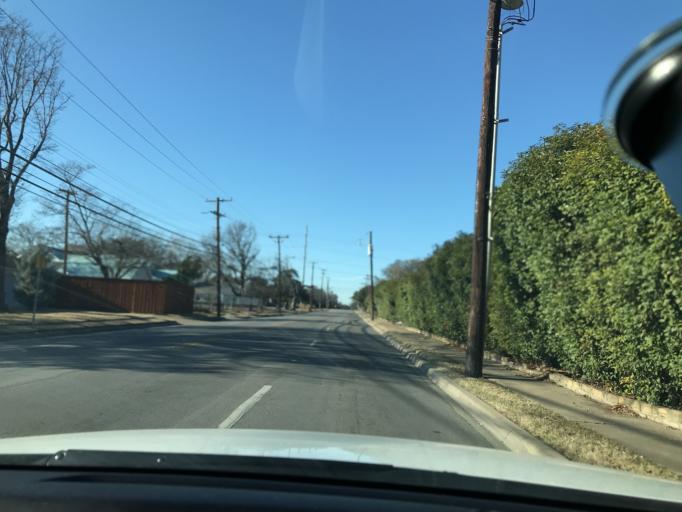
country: US
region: Texas
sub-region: Dallas County
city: Garland
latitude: 32.8312
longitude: -96.6882
